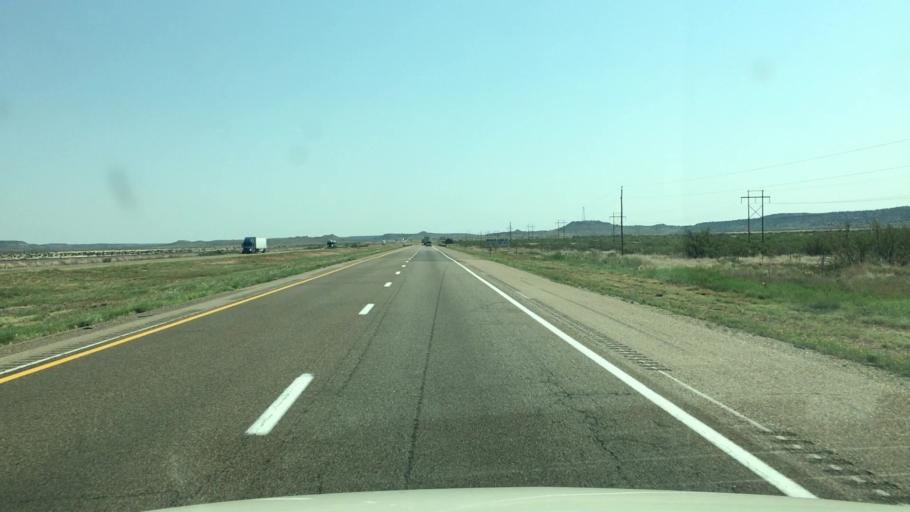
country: US
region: New Mexico
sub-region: Quay County
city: Tucumcari
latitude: 35.1161
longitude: -103.9877
